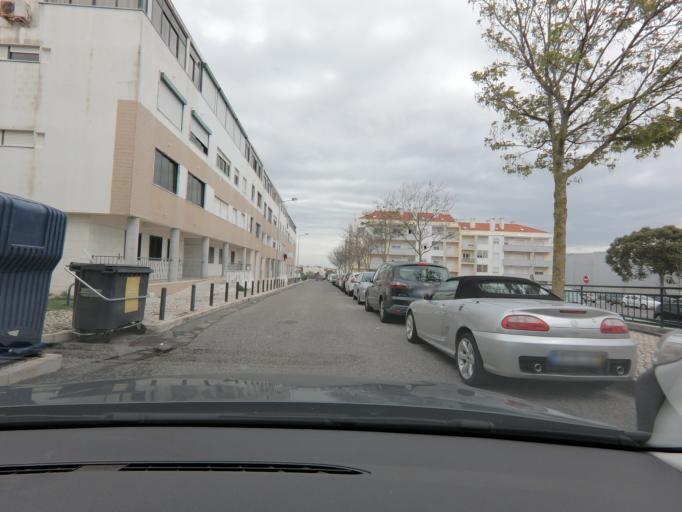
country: PT
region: Lisbon
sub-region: Cascais
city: Sao Domingos de Rana
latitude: 38.7263
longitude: -9.3286
